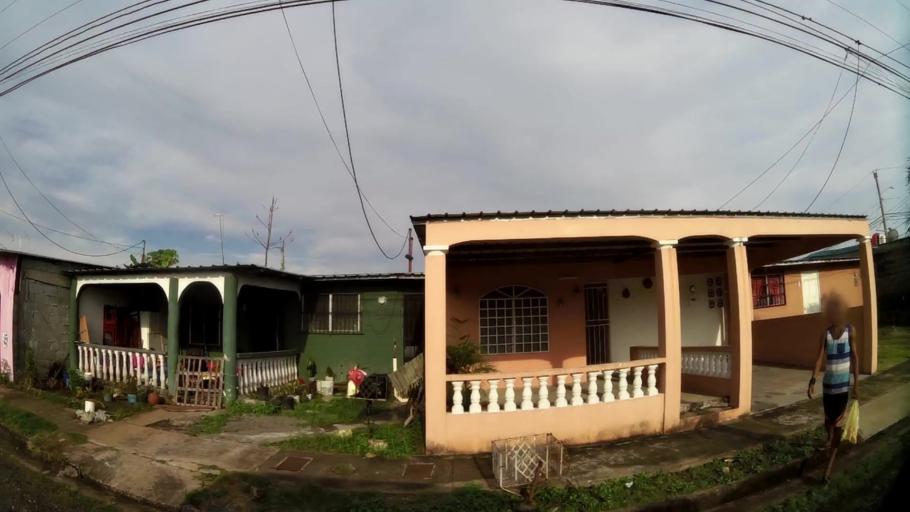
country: PA
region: Panama
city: Tocumen
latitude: 9.0774
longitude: -79.3607
